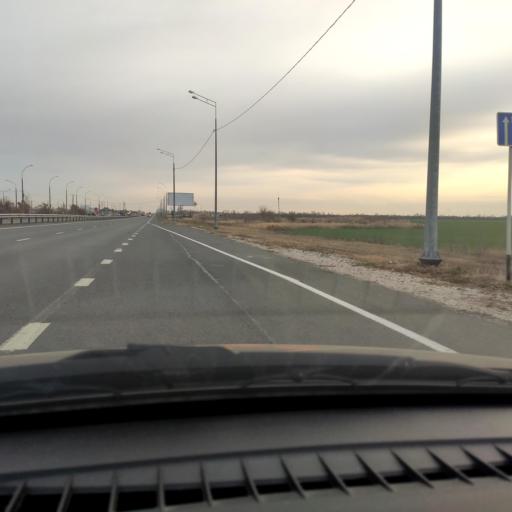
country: RU
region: Samara
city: Tol'yatti
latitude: 53.5539
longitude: 49.3429
